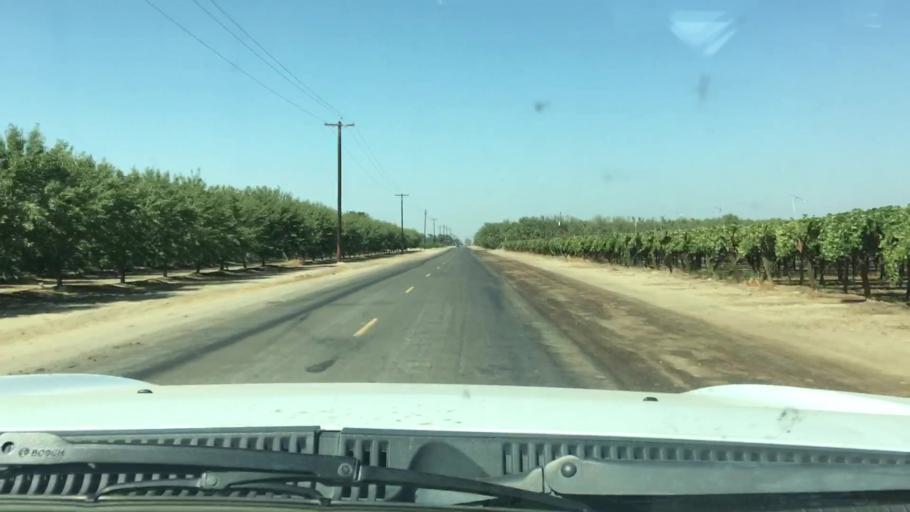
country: US
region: California
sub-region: Kern County
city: Shafter
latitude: 35.4940
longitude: -119.3139
